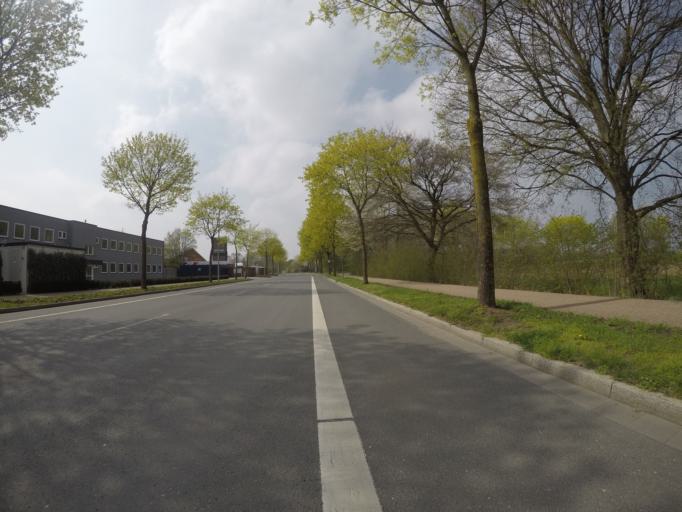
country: DE
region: North Rhine-Westphalia
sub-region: Regierungsbezirk Dusseldorf
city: Bocholt
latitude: 51.8150
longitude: 6.5409
